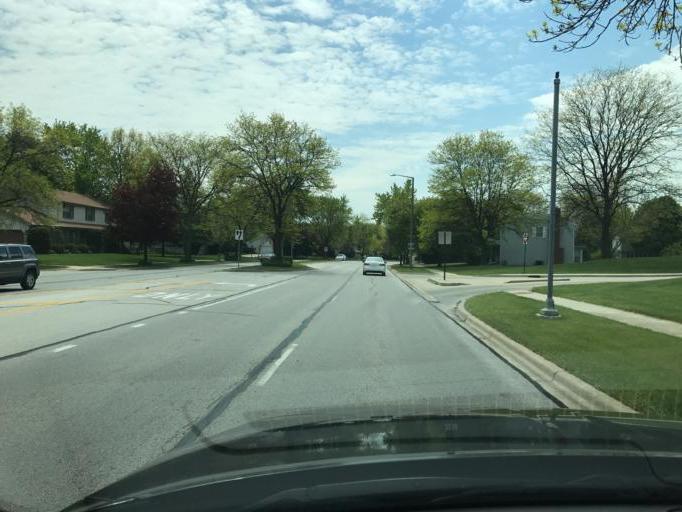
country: US
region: Illinois
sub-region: DuPage County
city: Naperville
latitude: 41.7592
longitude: -88.1130
